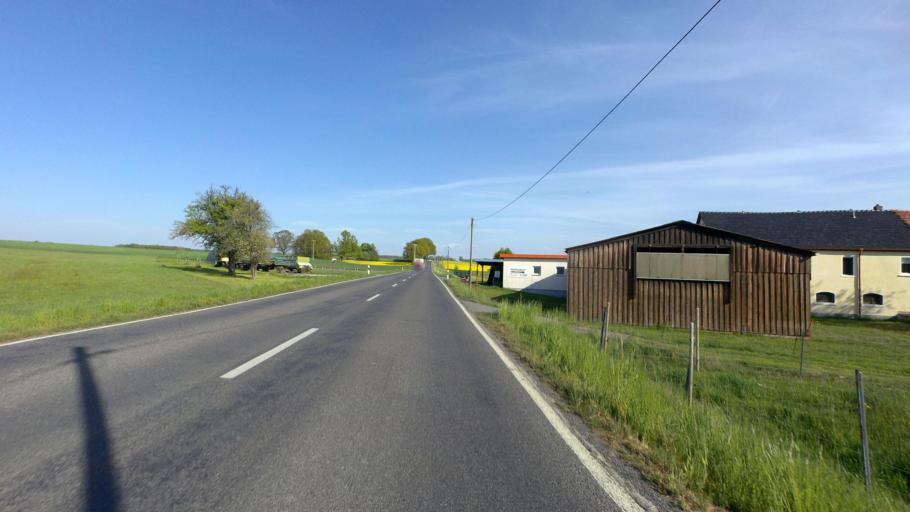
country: DE
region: Saxony
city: Arnsdorf
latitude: 51.0856
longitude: 14.0200
